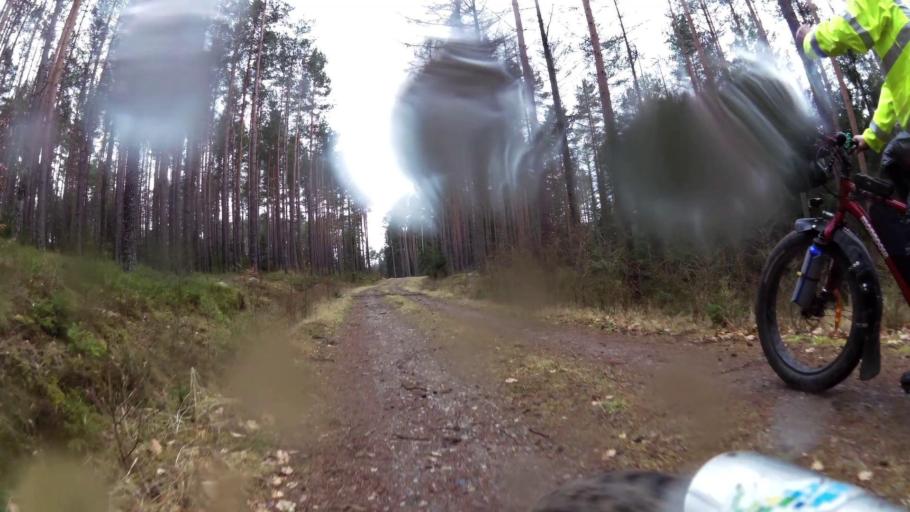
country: PL
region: Pomeranian Voivodeship
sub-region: Powiat bytowski
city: Trzebielino
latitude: 54.0766
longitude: 17.0955
